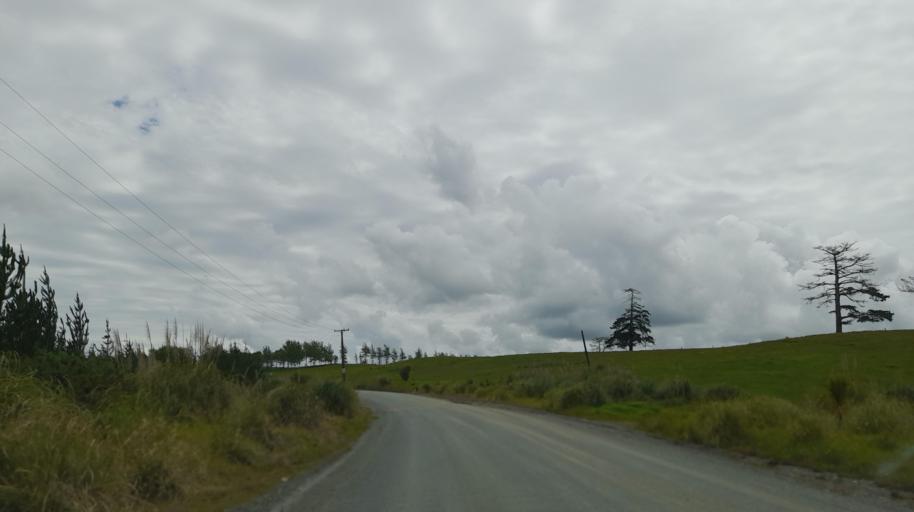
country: NZ
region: Auckland
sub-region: Auckland
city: Wellsford
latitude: -36.2330
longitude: 174.4415
